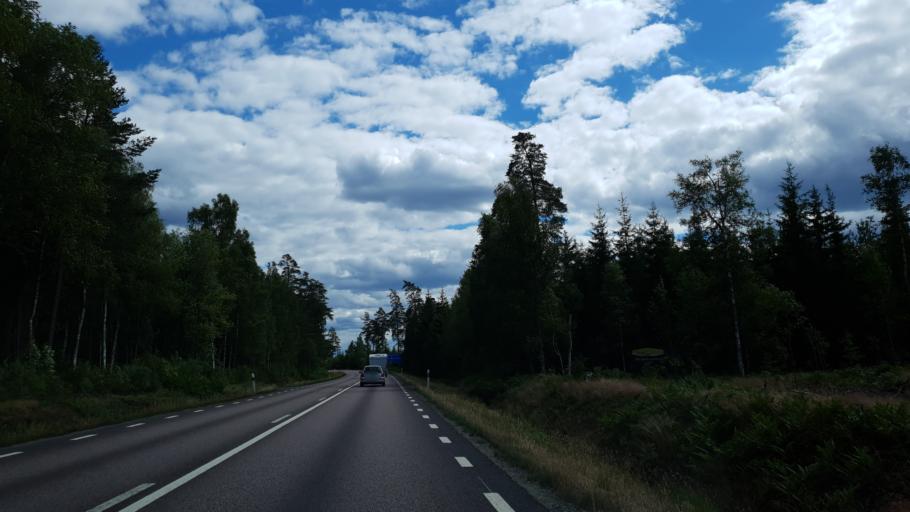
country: SE
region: Kronoberg
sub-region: Lessebo Kommun
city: Lessebo
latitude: 56.8365
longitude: 15.3925
